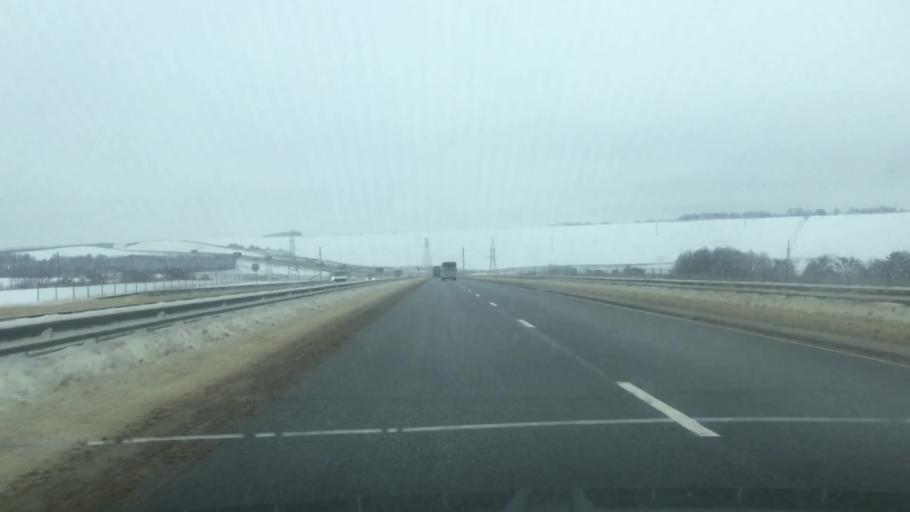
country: RU
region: Tula
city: Kazachka
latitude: 53.2813
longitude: 38.1796
